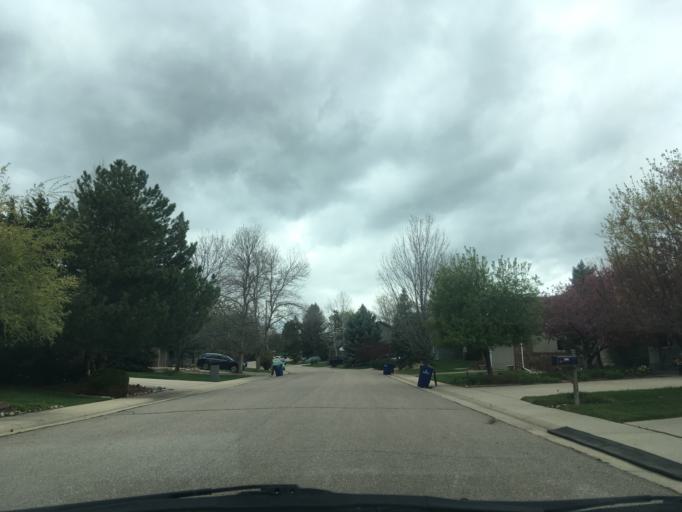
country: US
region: Colorado
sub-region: Boulder County
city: Louisville
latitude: 40.0224
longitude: -105.1249
